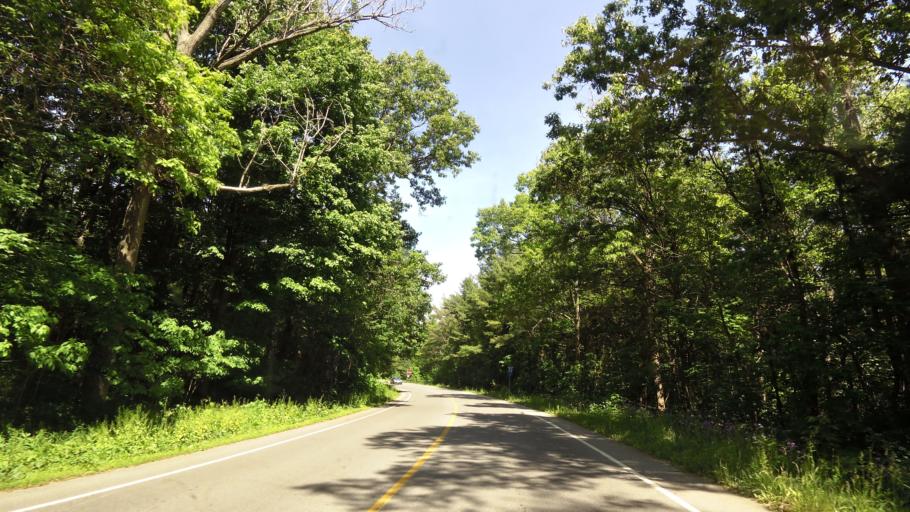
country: CA
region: Ontario
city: Norfolk County
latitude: 42.6976
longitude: -80.3375
